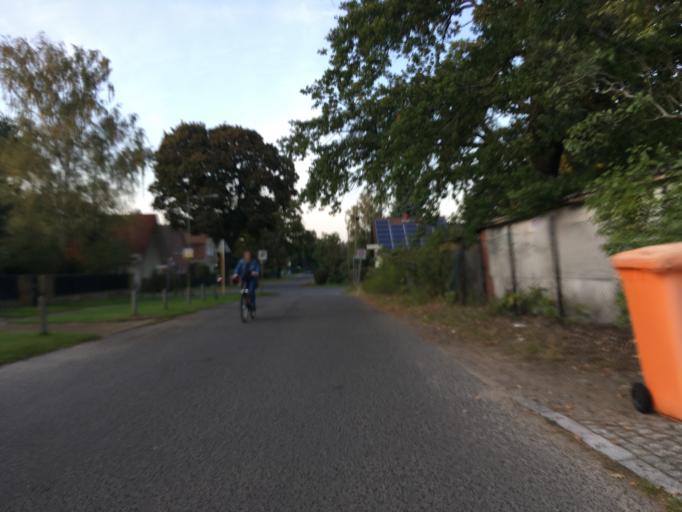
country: DE
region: Berlin
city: Biesdorf
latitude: 52.4922
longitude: 13.5586
